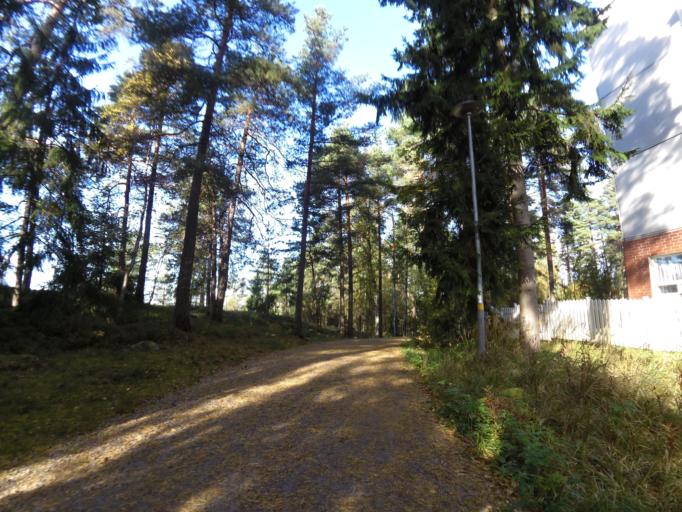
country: FI
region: Uusimaa
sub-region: Helsinki
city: Espoo
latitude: 60.1487
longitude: 24.6350
